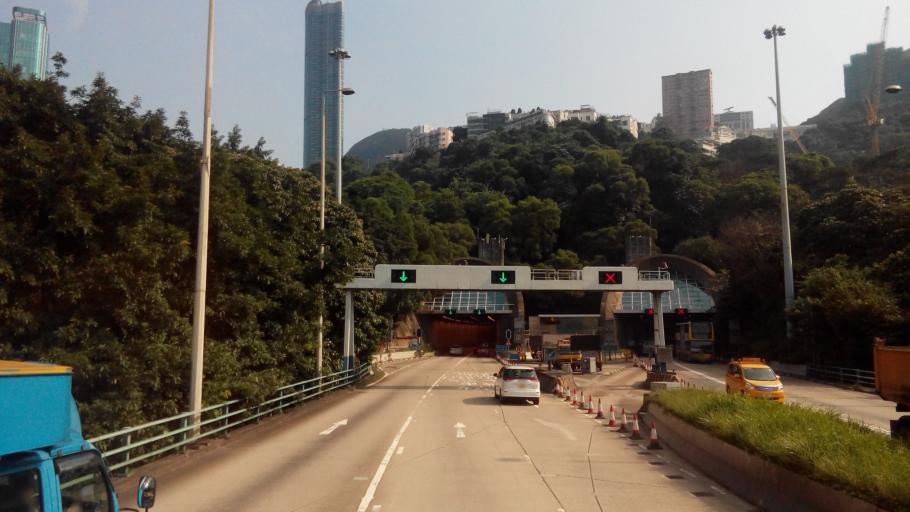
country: HK
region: Wanchai
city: Wan Chai
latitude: 22.2715
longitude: 114.1803
